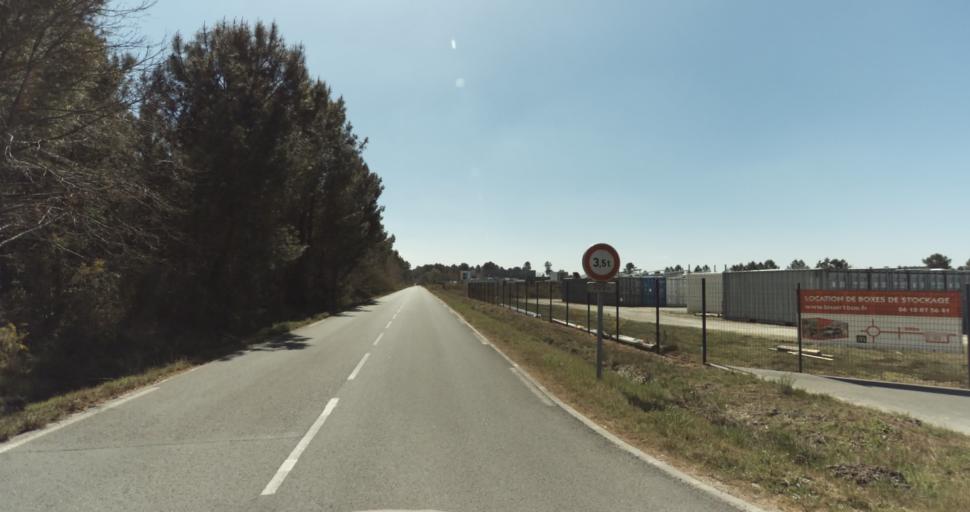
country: FR
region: Aquitaine
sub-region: Departement de la Gironde
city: Martignas-sur-Jalle
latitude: 44.8070
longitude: -0.7523
